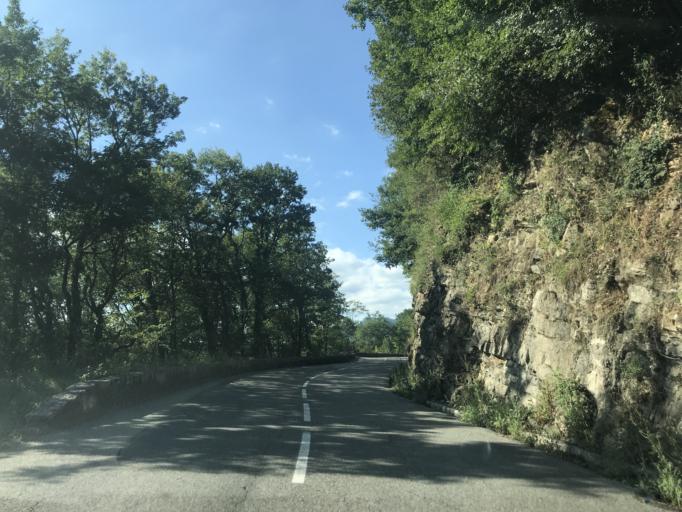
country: FR
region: Rhone-Alpes
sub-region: Departement de l'Ain
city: Culoz
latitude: 45.7936
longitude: 5.7857
